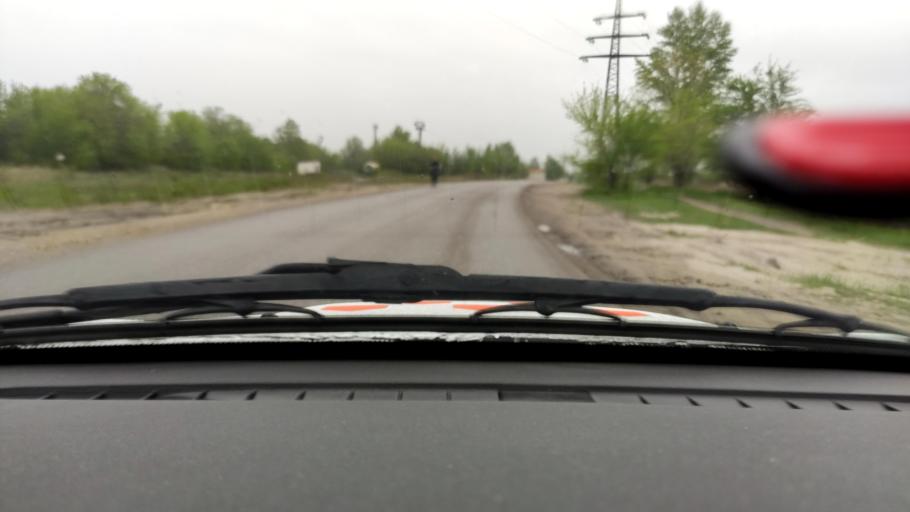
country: RU
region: Voronezj
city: Strelitsa
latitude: 51.6186
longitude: 38.9070
